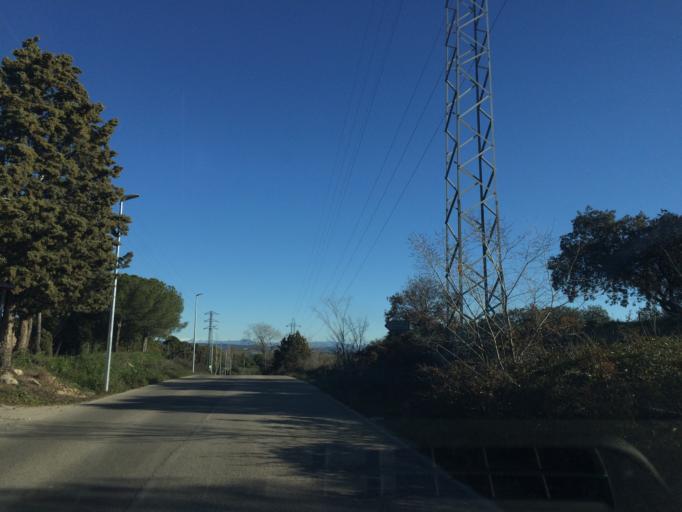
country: ES
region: Madrid
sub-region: Provincia de Madrid
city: Tres Cantos
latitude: 40.6052
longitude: -3.6885
